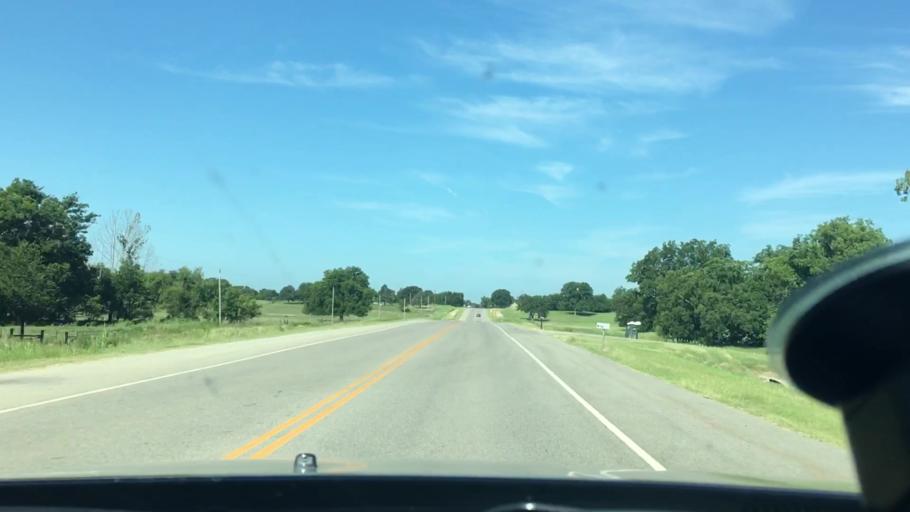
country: US
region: Oklahoma
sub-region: Johnston County
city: Tishomingo
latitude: 34.2742
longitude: -96.5414
